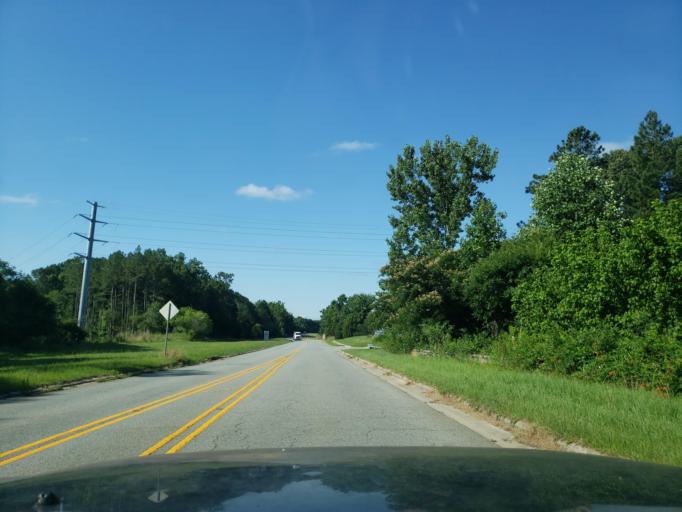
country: US
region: North Carolina
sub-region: Durham County
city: Durham
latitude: 35.9380
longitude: -78.8787
